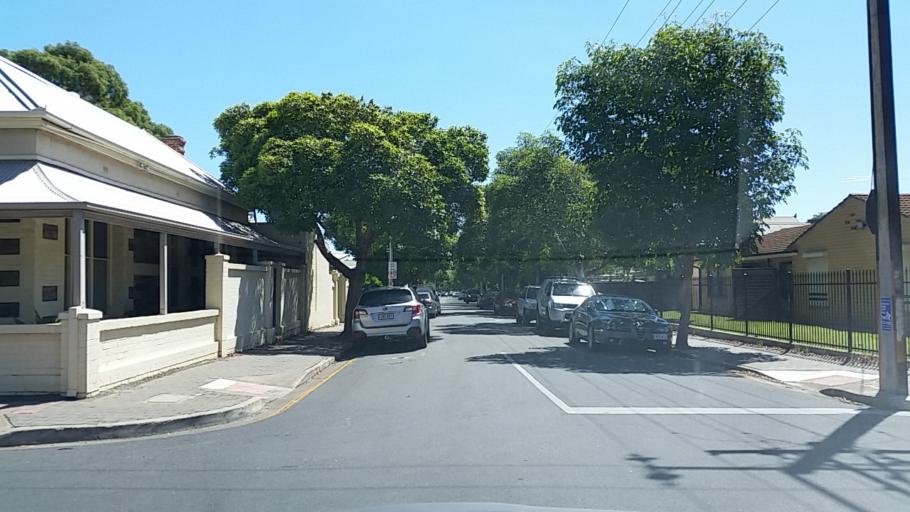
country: AU
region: South Australia
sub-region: Unley
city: Fullarton
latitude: -34.9450
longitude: 138.6186
